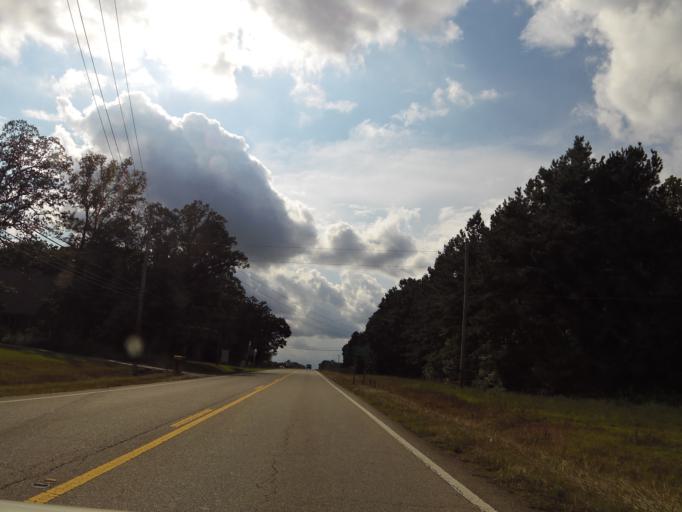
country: US
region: Mississippi
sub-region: Alcorn County
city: Farmington
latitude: 34.9816
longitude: -88.4738
